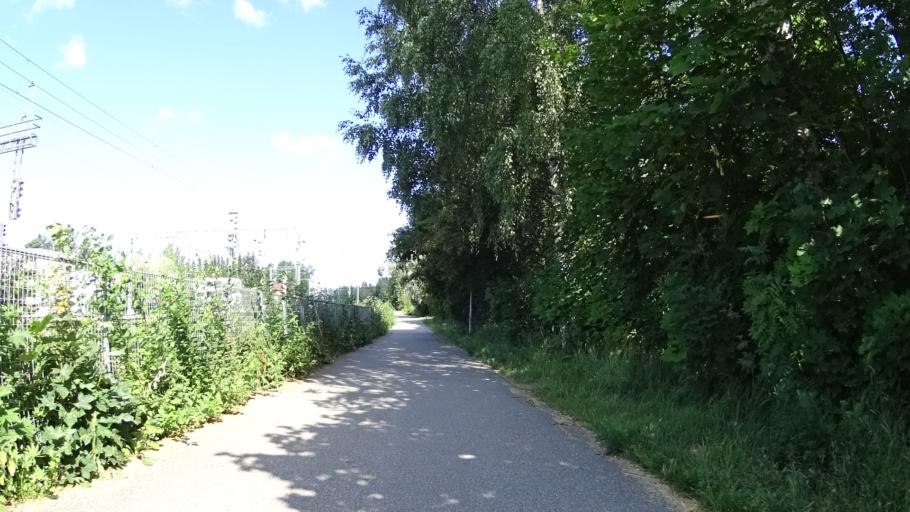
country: FI
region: Uusimaa
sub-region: Helsinki
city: Jaervenpaeae
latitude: 60.4671
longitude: 25.0988
